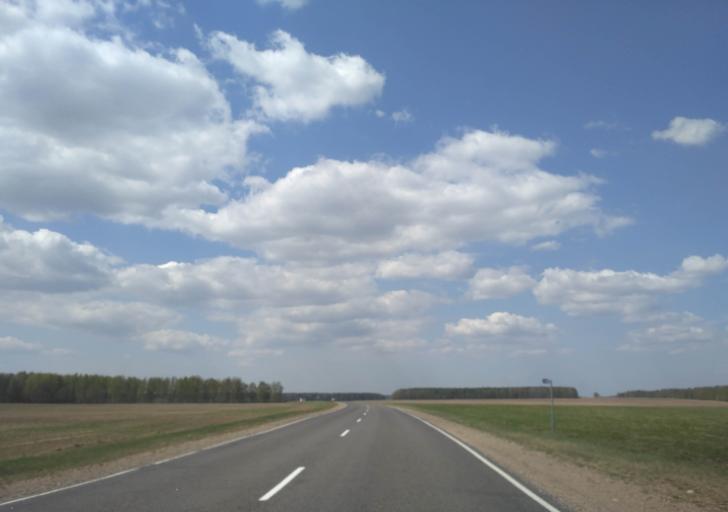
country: BY
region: Minsk
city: Vilyeyka
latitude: 54.5156
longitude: 27.0392
